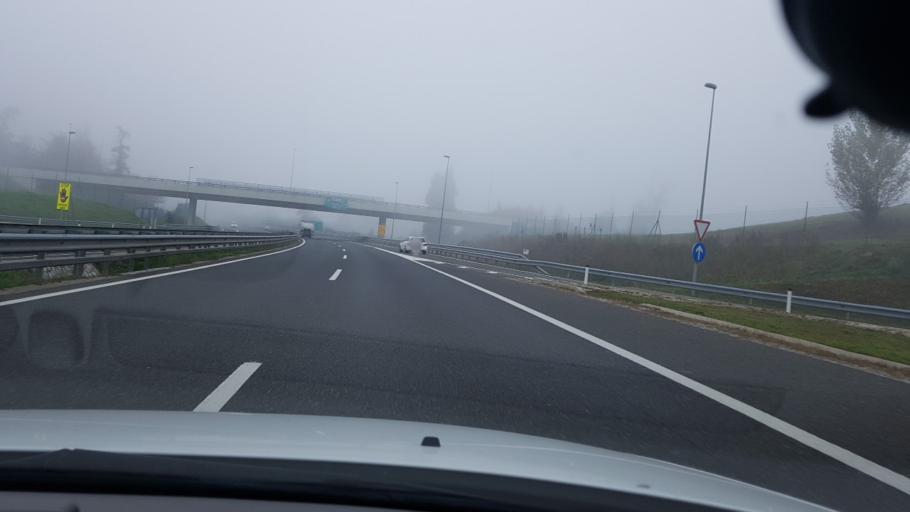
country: SI
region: Trebnje
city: Trebnje
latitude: 45.8975
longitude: 15.0558
